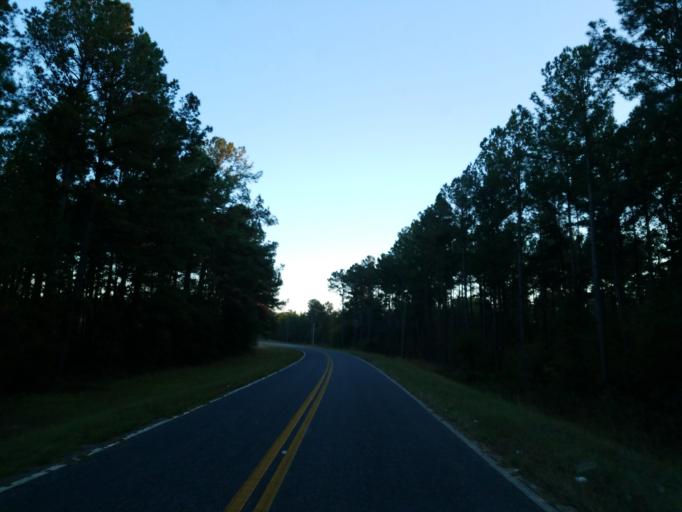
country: US
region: Georgia
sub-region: Ben Hill County
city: Fitzgerald
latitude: 31.6811
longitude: -83.4080
